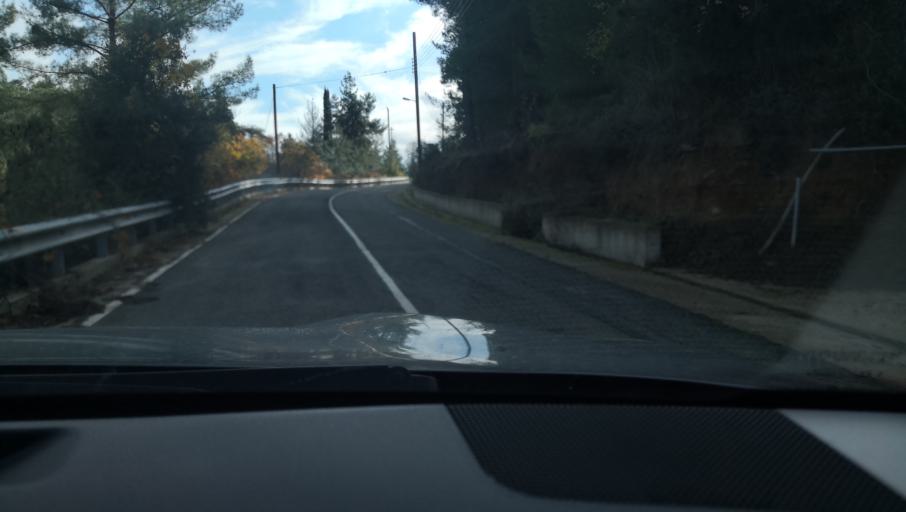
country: CY
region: Lefkosia
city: Lefka
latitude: 35.0156
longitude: 32.7294
